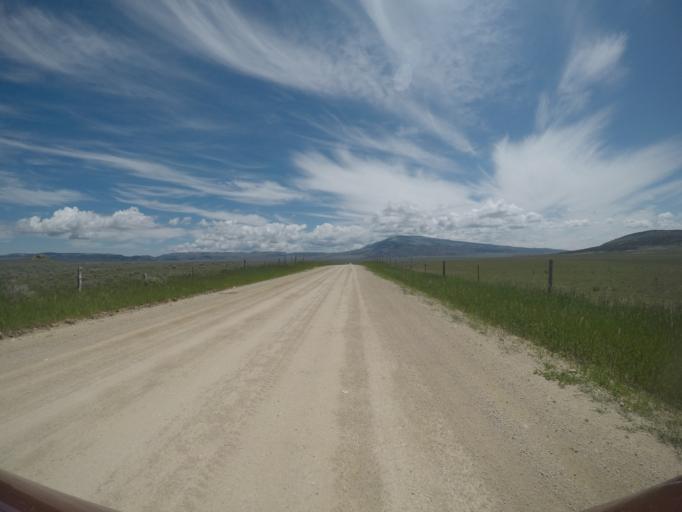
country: US
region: Wyoming
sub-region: Park County
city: Powell
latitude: 45.2051
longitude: -108.7582
